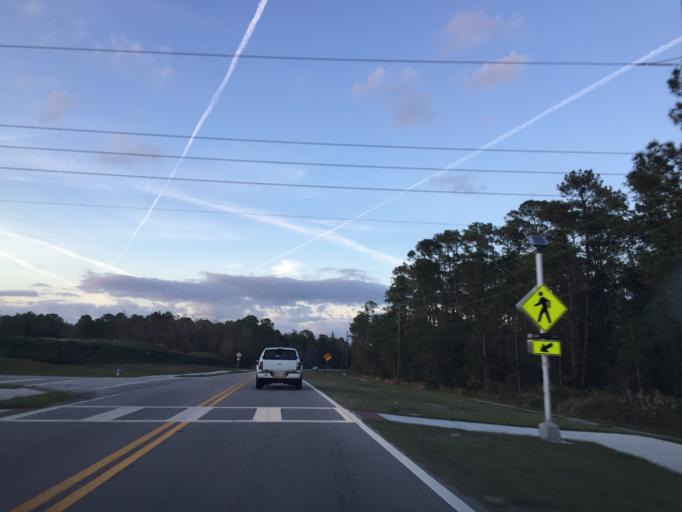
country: US
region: Florida
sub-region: Seminole County
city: Oviedo
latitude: 28.6666
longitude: -81.1768
